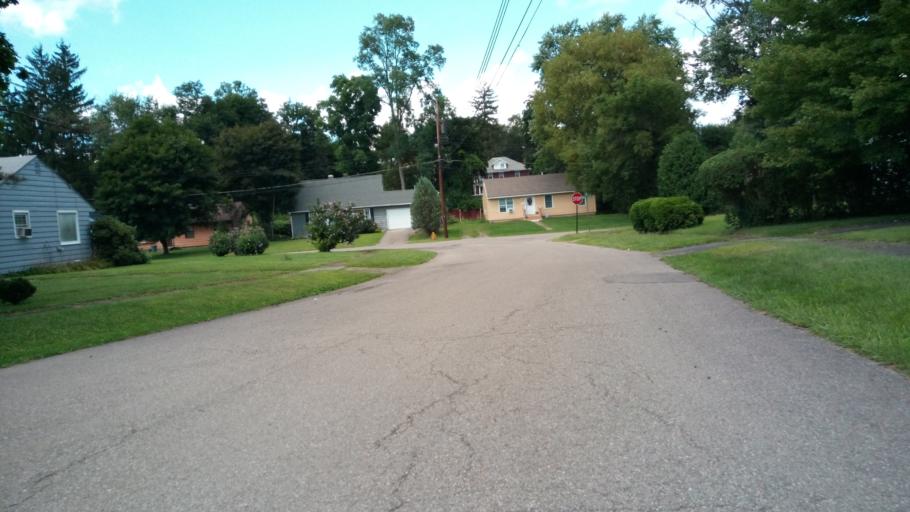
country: US
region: New York
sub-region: Chemung County
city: West Elmira
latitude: 42.0795
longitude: -76.8299
